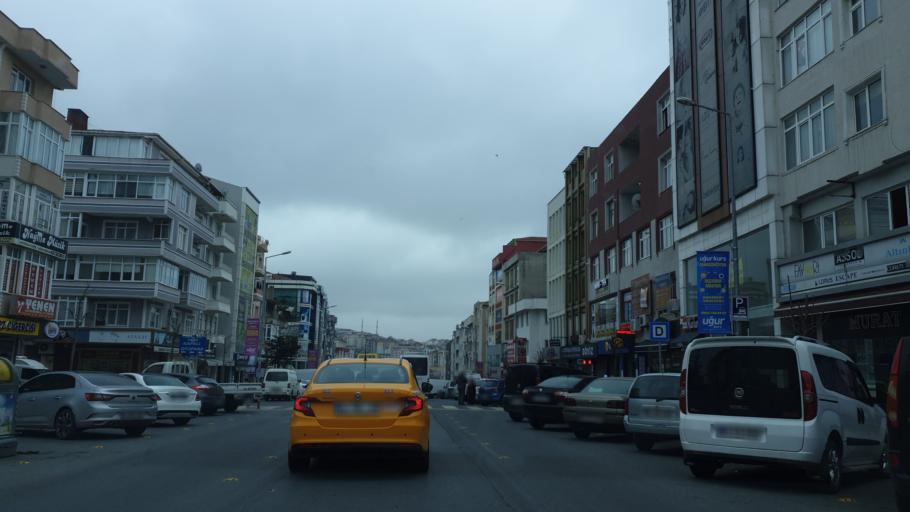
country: TR
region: Tekirdag
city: Cerkezkoey
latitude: 41.2850
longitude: 27.9999
